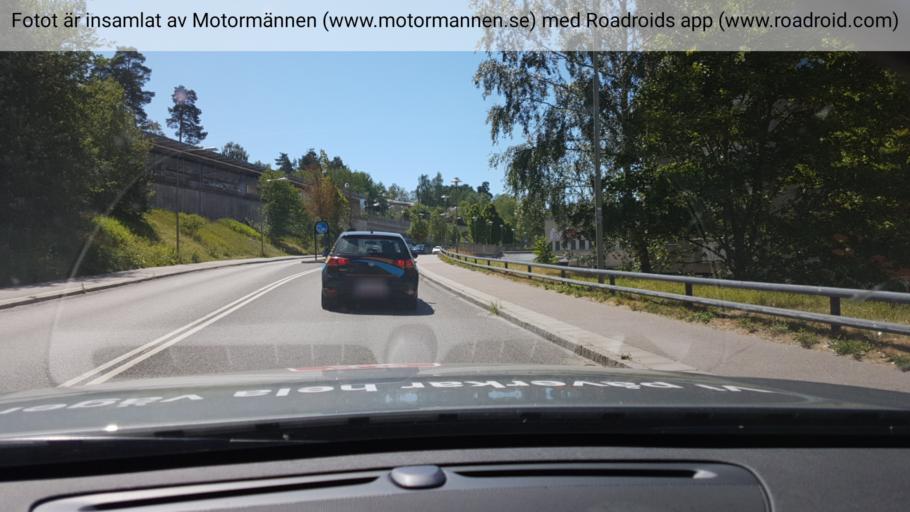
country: SE
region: Stockholm
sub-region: Stockholms Kommun
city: Arsta
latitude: 59.2576
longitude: 18.0294
